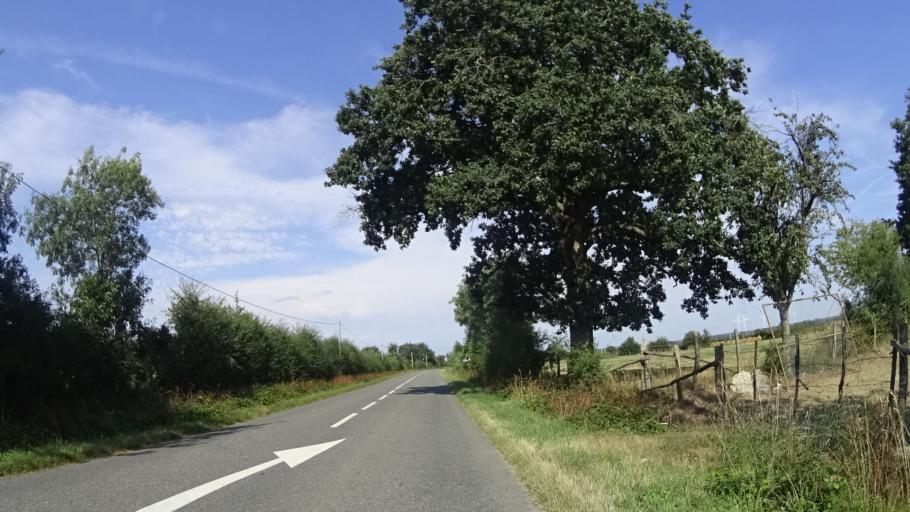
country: FR
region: Pays de la Loire
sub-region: Departement de la Loire-Atlantique
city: Abbaretz
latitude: 47.5103
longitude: -1.5331
